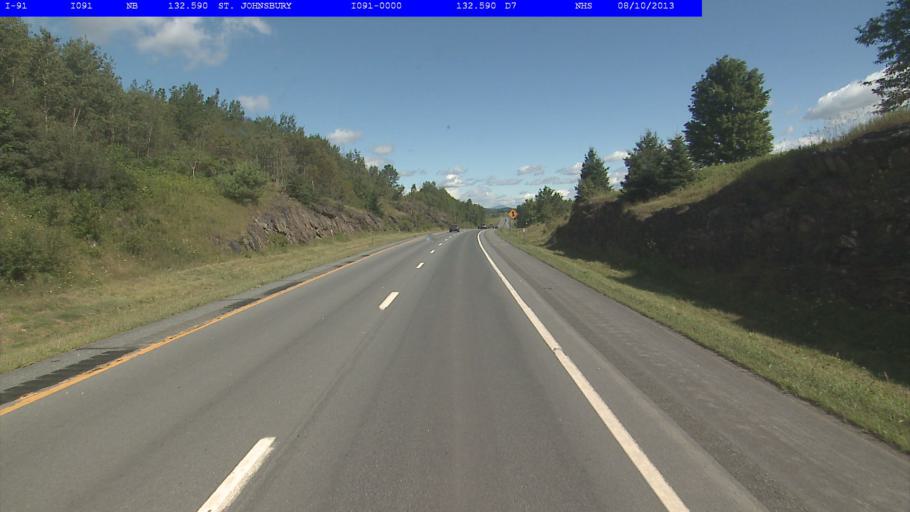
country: US
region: Vermont
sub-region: Caledonia County
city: St Johnsbury
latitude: 44.4542
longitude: -72.0243
